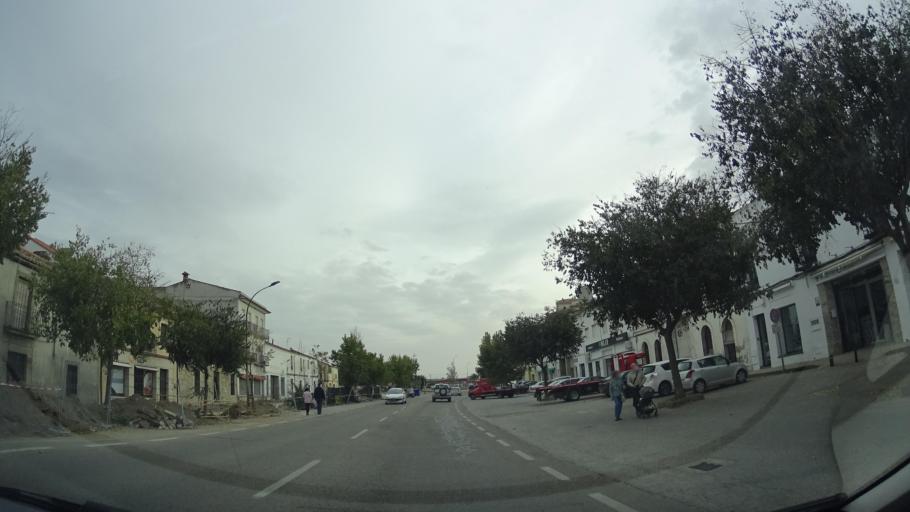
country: ES
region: Extremadura
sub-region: Provincia de Caceres
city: Trujillo
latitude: 39.4544
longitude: -5.8807
